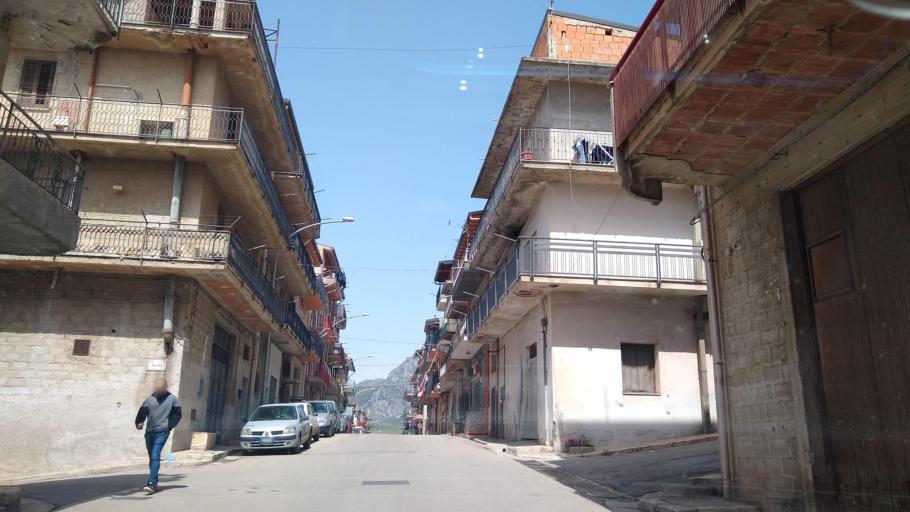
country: IT
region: Sicily
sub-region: Palermo
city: San Giuseppe Jato
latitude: 37.9713
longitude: 13.1801
